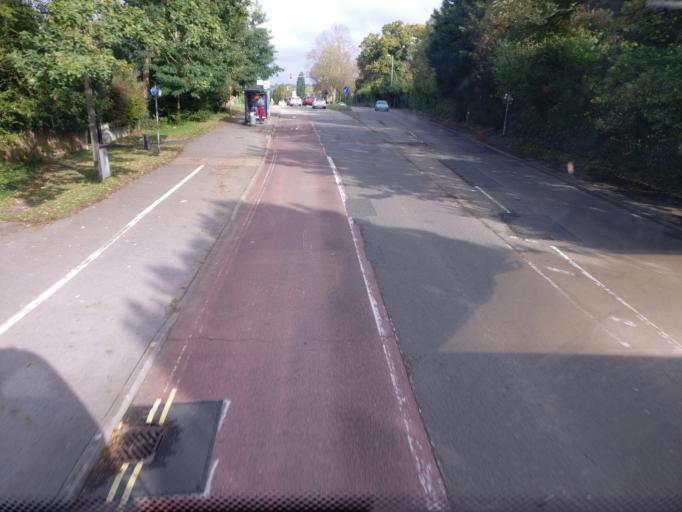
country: GB
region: England
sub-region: Hampshire
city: Farnborough
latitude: 51.3035
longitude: -0.7517
